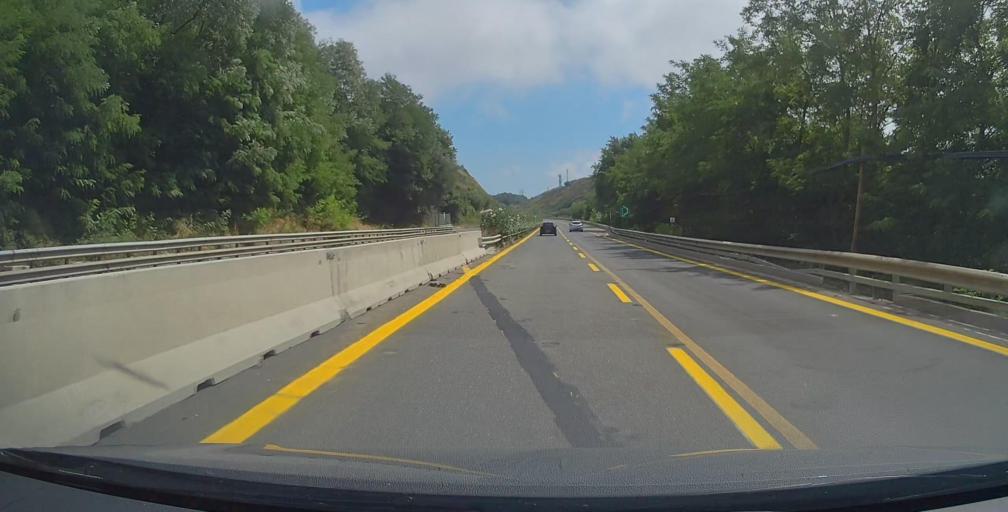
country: IT
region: Calabria
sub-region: Provincia di Vibo-Valentia
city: Sant'Onofrio
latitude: 38.7158
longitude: 16.1543
